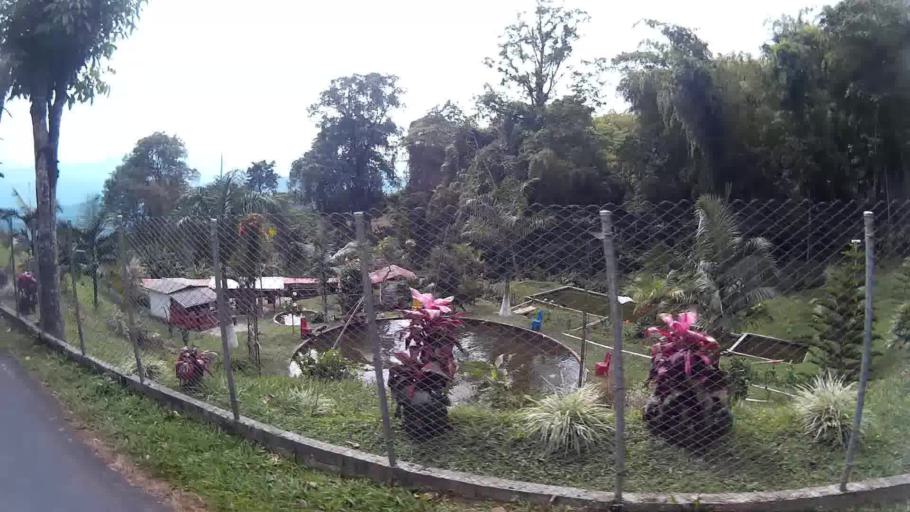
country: CO
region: Risaralda
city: Marsella
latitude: 4.8850
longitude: -75.7517
